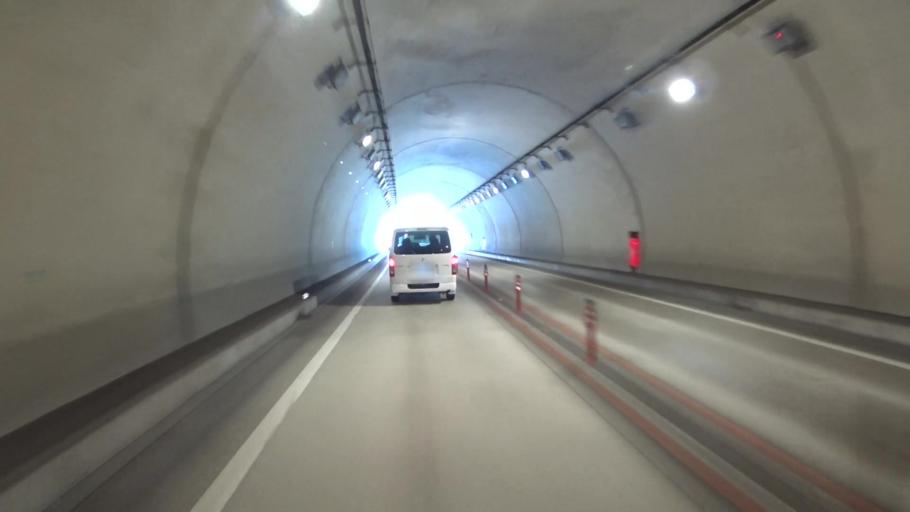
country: JP
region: Kyoto
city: Miyazu
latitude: 35.5456
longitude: 135.1510
